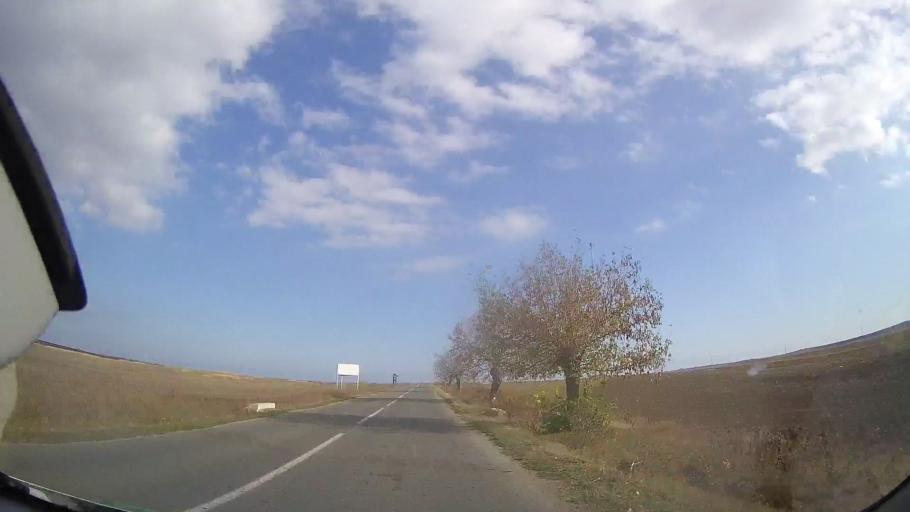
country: RO
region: Constanta
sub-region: Comuna Pecineaga
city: Pecineaga
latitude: 43.8973
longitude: 28.5134
